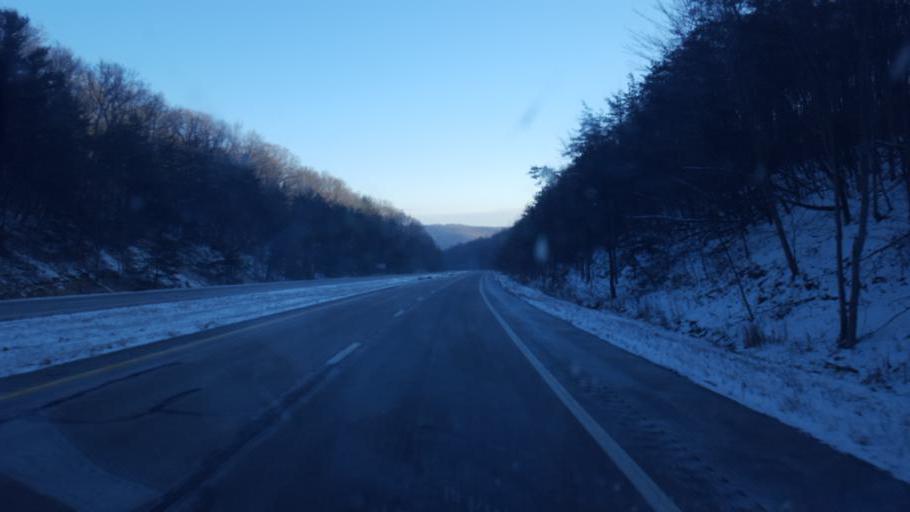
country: US
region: Ohio
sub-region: Adams County
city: Peebles
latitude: 39.0239
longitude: -83.2736
